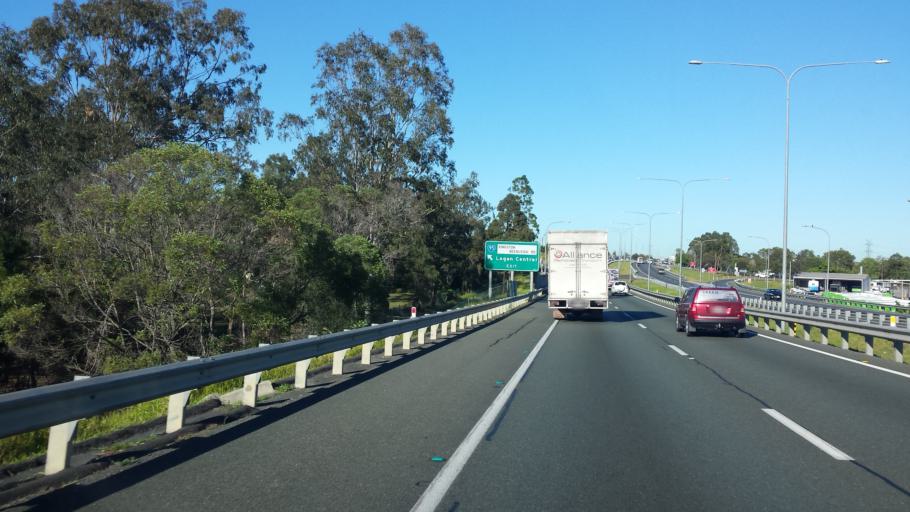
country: AU
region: Queensland
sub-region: Logan
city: Waterford West
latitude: -27.6674
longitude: 153.1283
